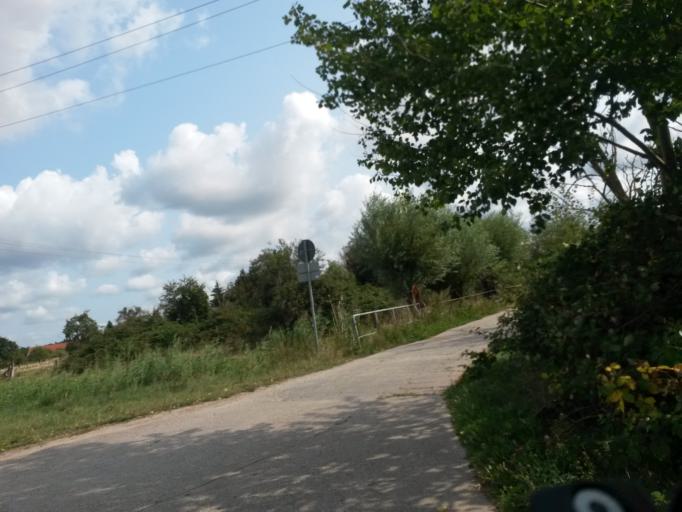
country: DE
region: Saxony-Anhalt
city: Arneburg
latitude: 52.6477
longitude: 12.0389
